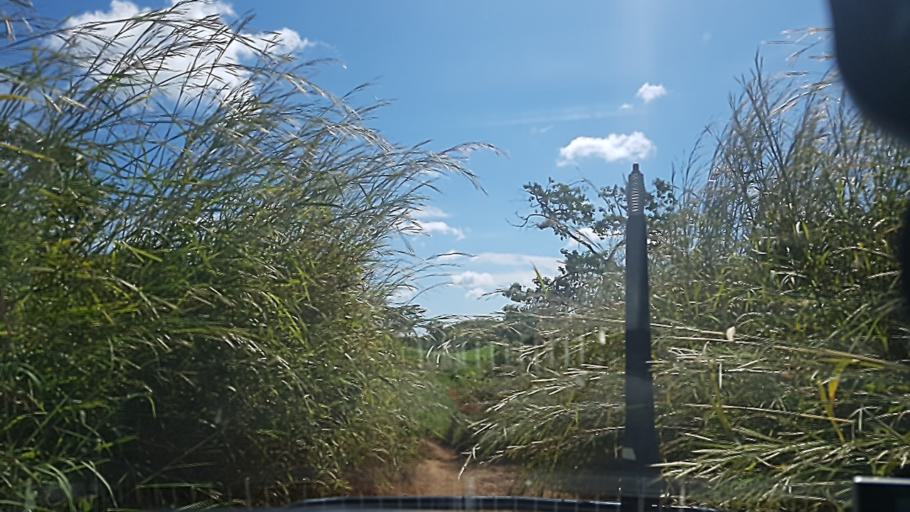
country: NI
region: Granada
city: Nandaime
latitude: 11.5771
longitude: -86.0943
